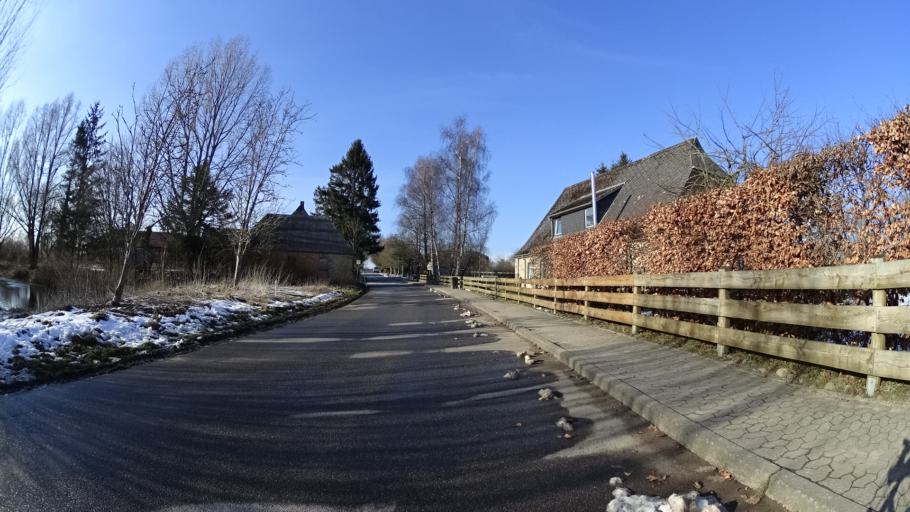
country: DE
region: Schleswig-Holstein
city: Martensrade
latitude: 54.2722
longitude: 10.3913
